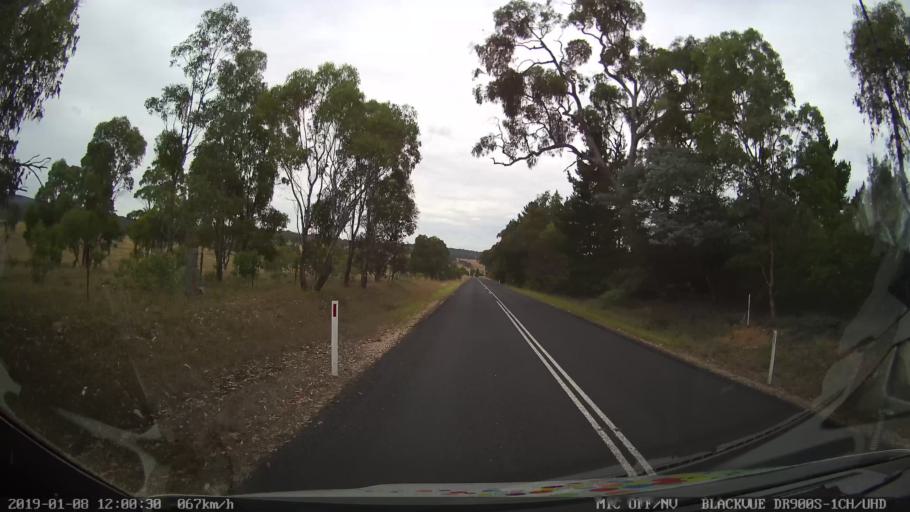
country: AU
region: New South Wales
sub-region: Armidale Dumaresq
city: Armidale
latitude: -30.4605
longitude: 151.6019
